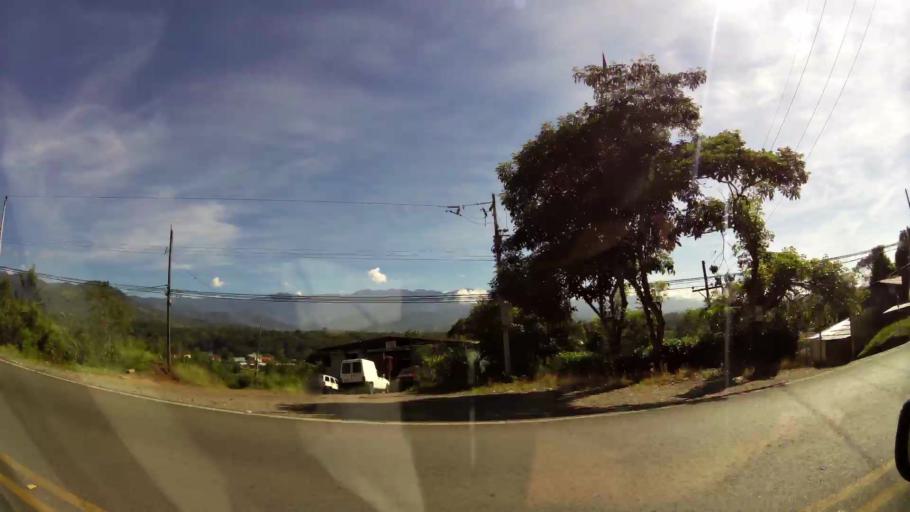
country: CR
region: San Jose
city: San Isidro
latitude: 9.3904
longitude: -83.7071
